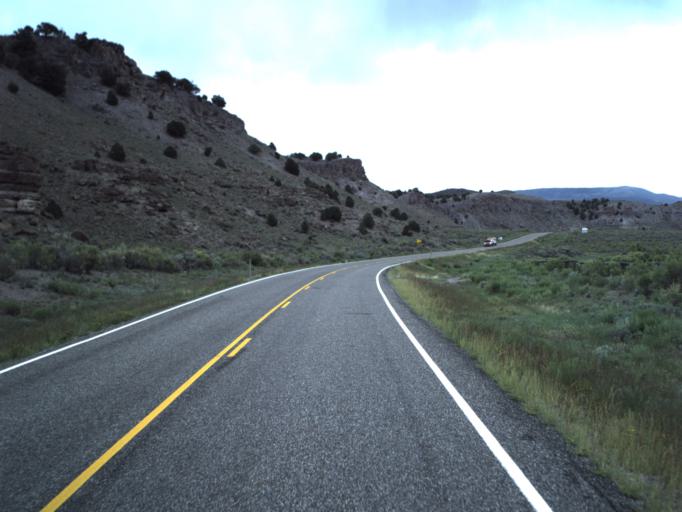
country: US
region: Utah
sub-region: Piute County
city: Junction
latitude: 38.1779
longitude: -112.0739
